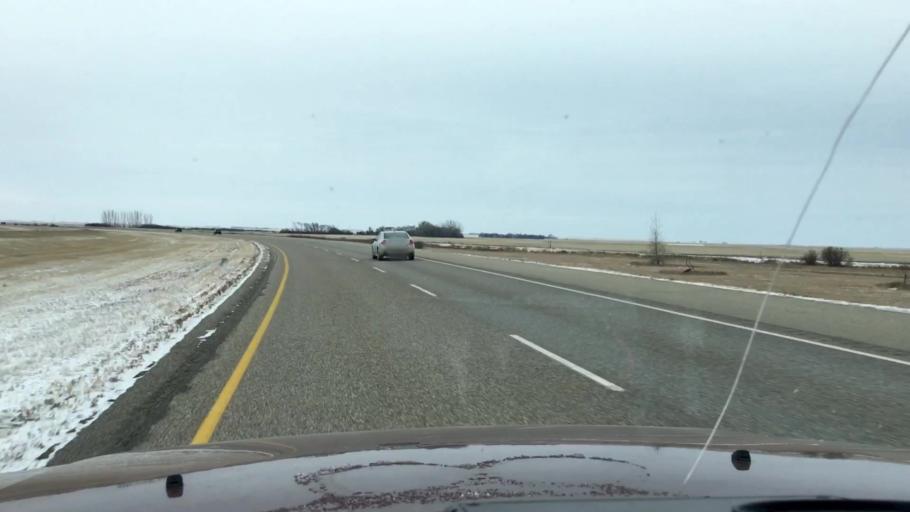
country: CA
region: Saskatchewan
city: Watrous
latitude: 51.1470
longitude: -105.9070
